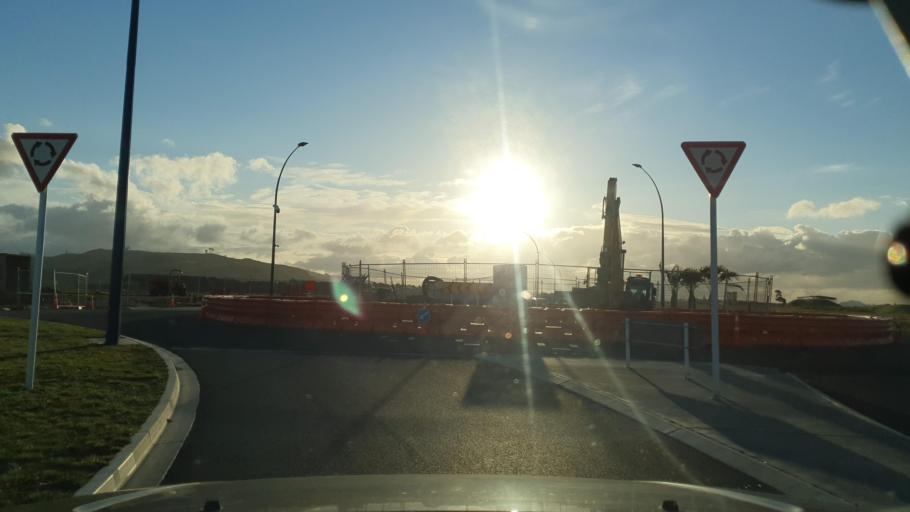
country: NZ
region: Bay of Plenty
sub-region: Western Bay of Plenty District
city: Maketu
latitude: -37.7258
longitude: 176.3290
